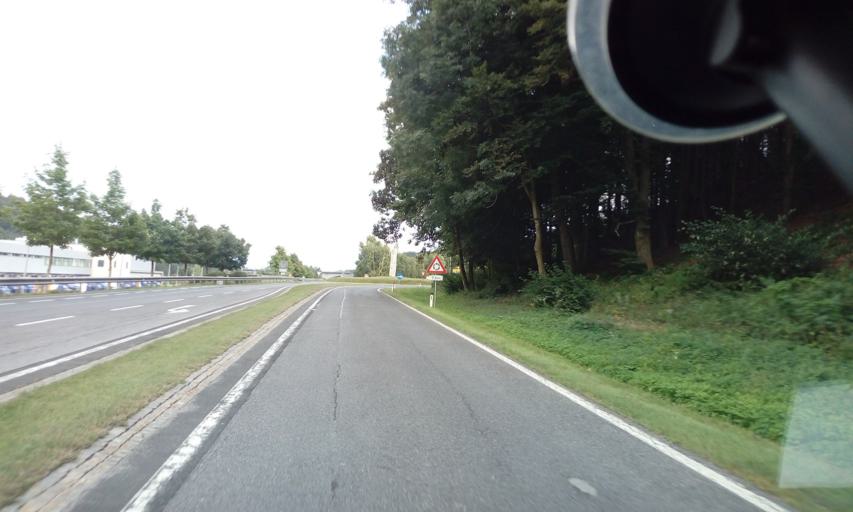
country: AT
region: Carinthia
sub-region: Villach Stadt
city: Villach
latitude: 46.6482
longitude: 13.7921
